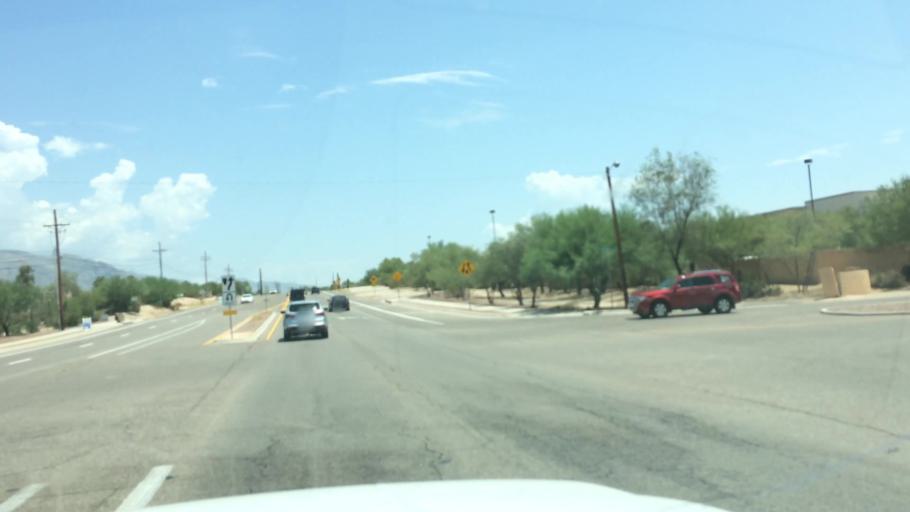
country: US
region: Arizona
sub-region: Pima County
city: Casas Adobes
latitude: 32.3231
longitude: -111.0082
